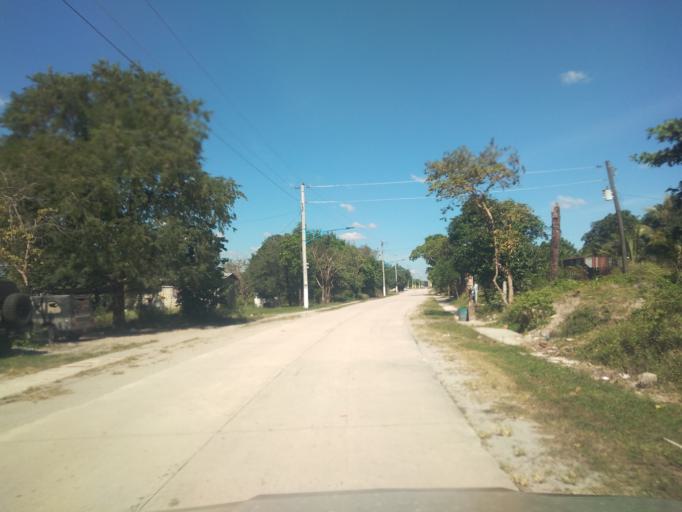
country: PH
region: Central Luzon
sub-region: Province of Pampanga
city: Balas
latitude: 15.0426
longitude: 120.6147
